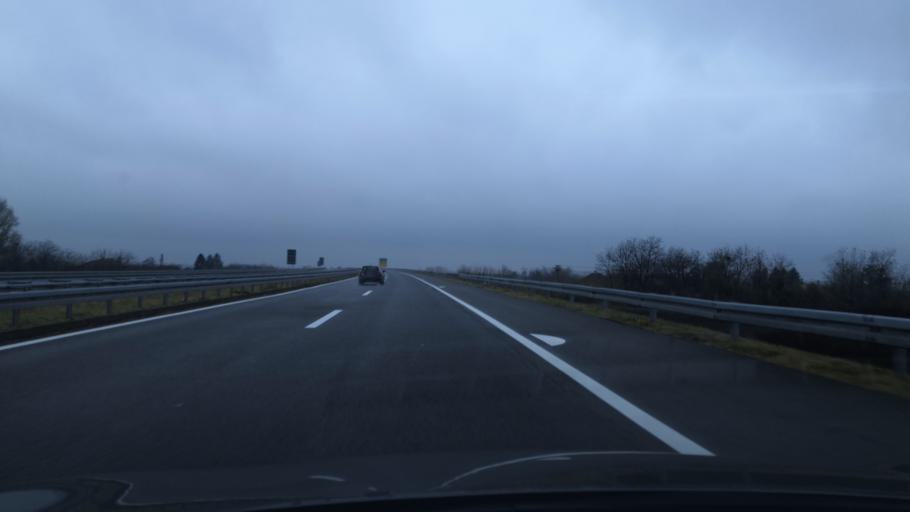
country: HU
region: Csongrad
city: Asotthalom
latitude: 46.1162
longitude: 19.8028
